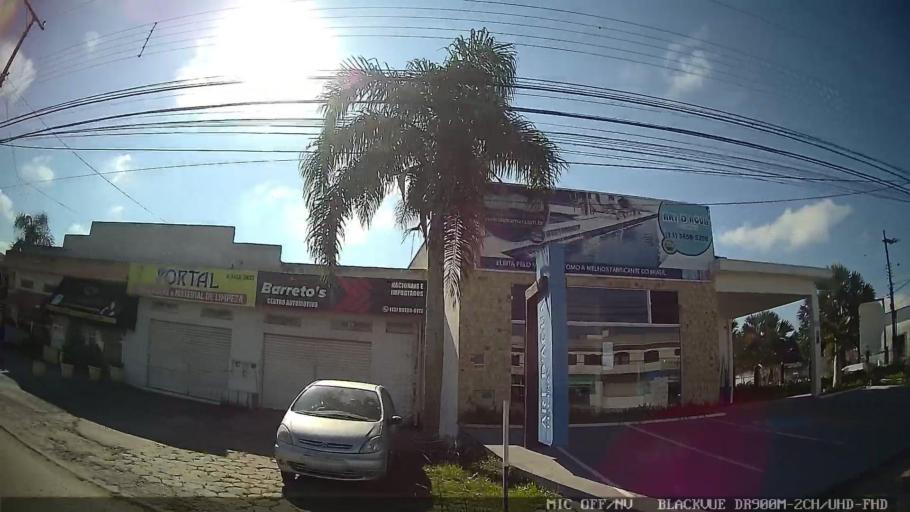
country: BR
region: Sao Paulo
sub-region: Peruibe
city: Peruibe
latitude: -24.2857
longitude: -46.9559
